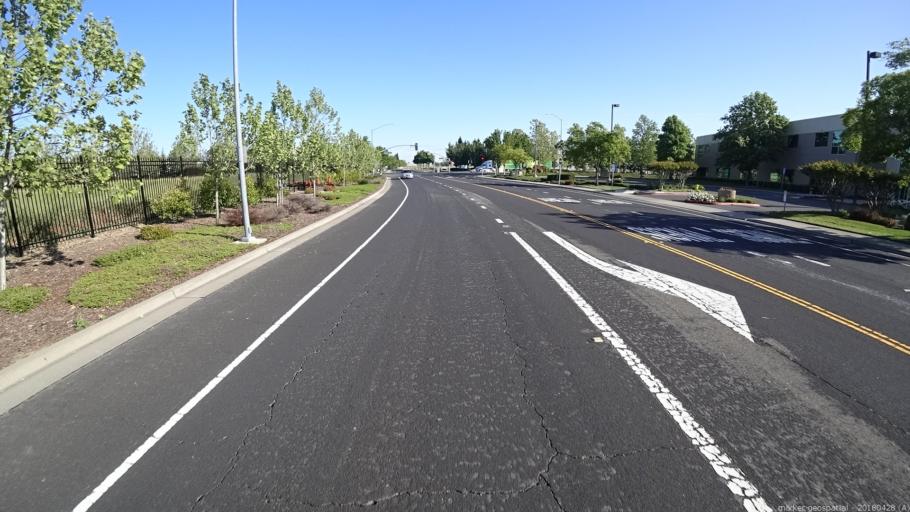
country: US
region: California
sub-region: Yolo County
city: West Sacramento
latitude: 38.5544
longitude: -121.5629
